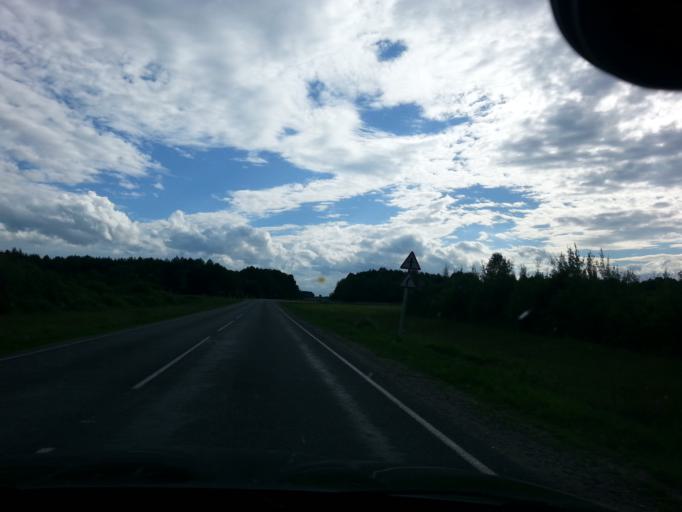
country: BY
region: Grodnenskaya
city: Astravyets
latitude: 54.8025
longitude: 26.1289
